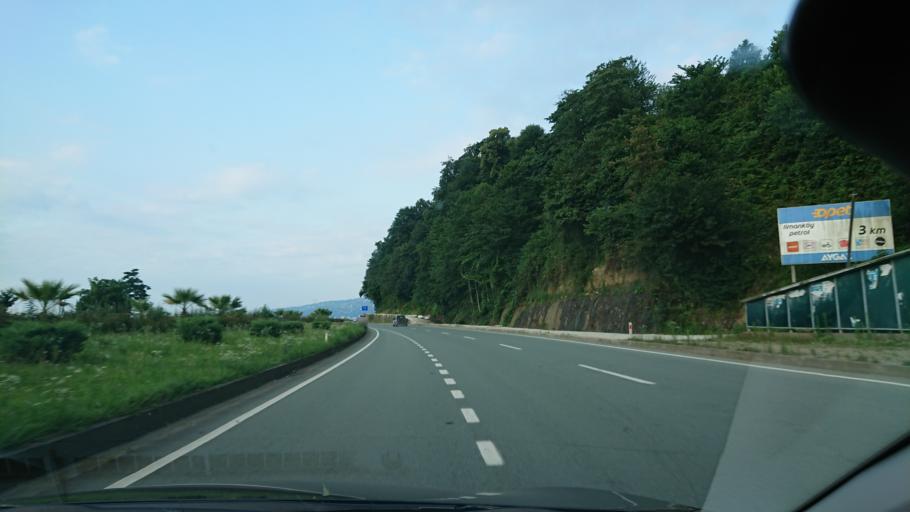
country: TR
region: Rize
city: Buyukkoy
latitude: 41.0680
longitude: 40.6526
